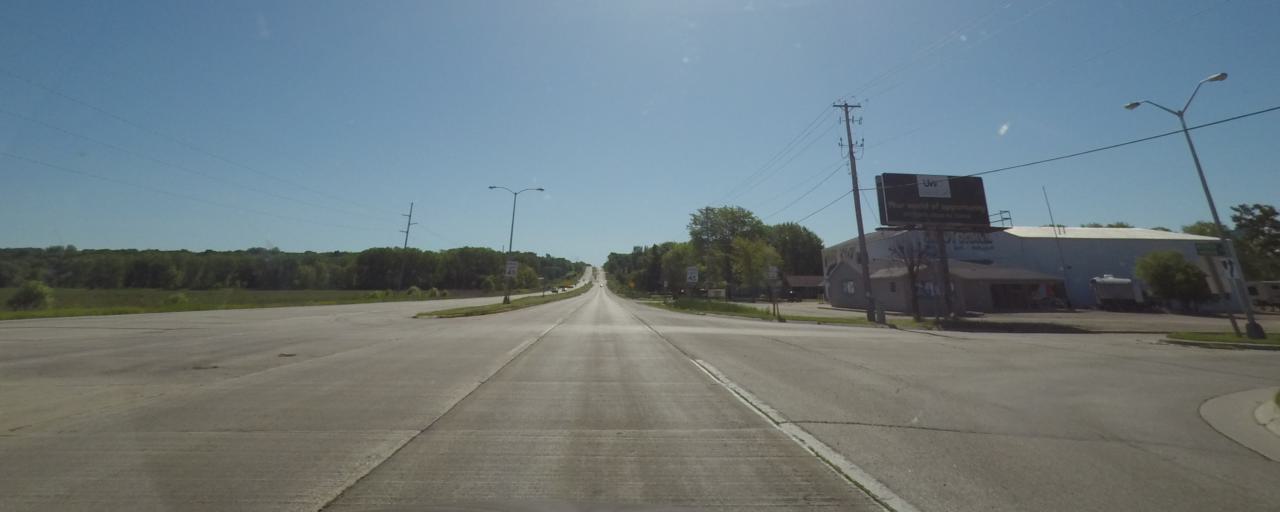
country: US
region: Wisconsin
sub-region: Fond du Lac County
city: Fond du Lac
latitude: 43.7837
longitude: -88.3969
